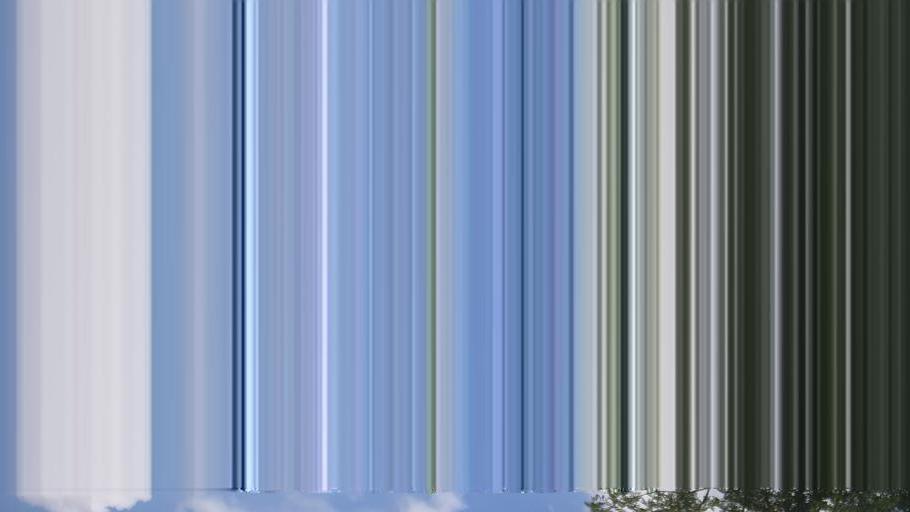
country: MY
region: Johor
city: Johor Bahru
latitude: 1.3871
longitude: 103.7563
